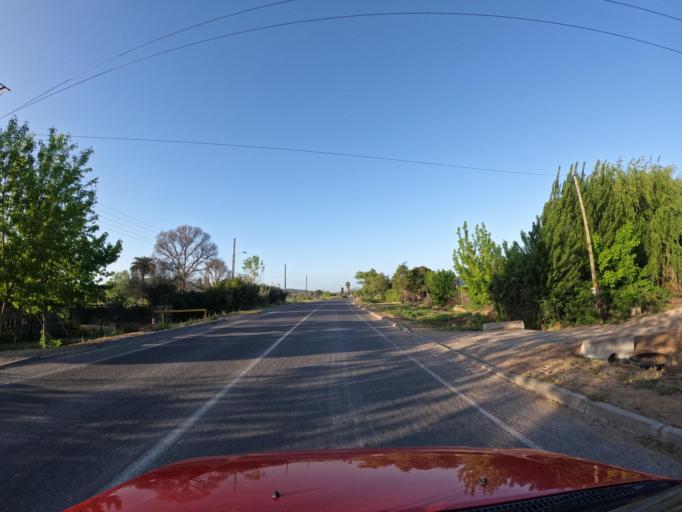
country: CL
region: O'Higgins
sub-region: Provincia de Colchagua
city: Santa Cruz
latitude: -34.3430
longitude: -71.4045
